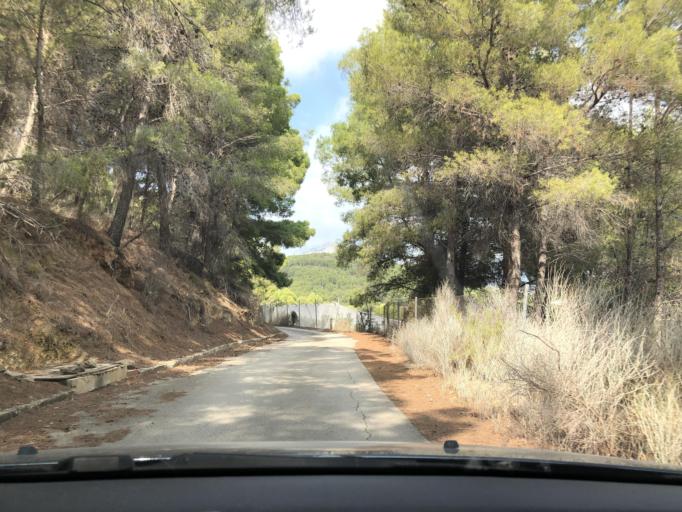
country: ES
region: Valencia
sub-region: Provincia de Alicante
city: Callosa d'En Sarria
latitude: 38.6349
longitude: -0.1076
